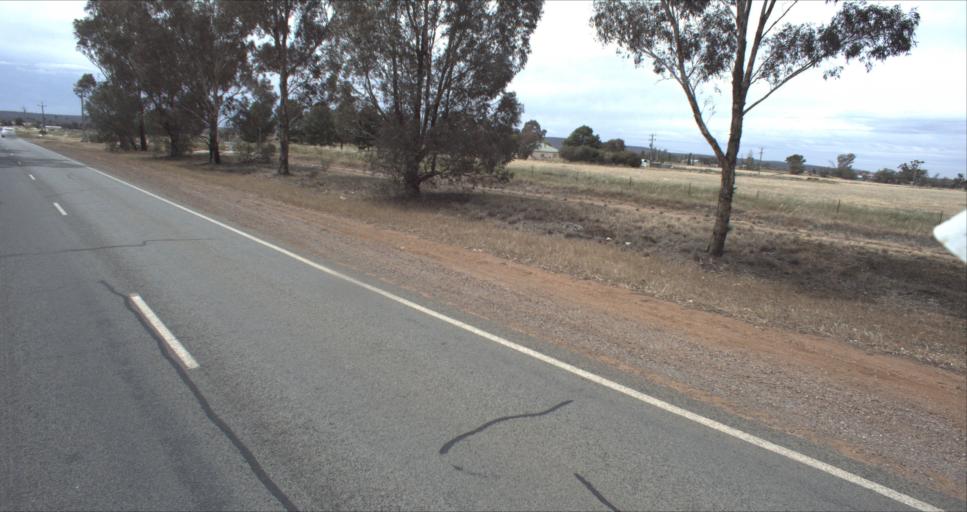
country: AU
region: New South Wales
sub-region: Leeton
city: Leeton
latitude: -34.5129
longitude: 146.4190
